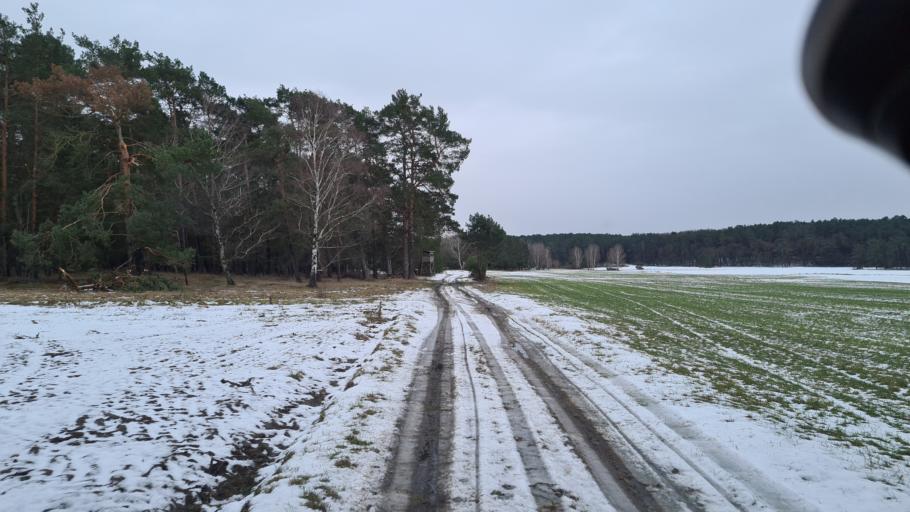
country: DE
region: Brandenburg
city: Schenkendobern
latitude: 51.9047
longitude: 14.5942
